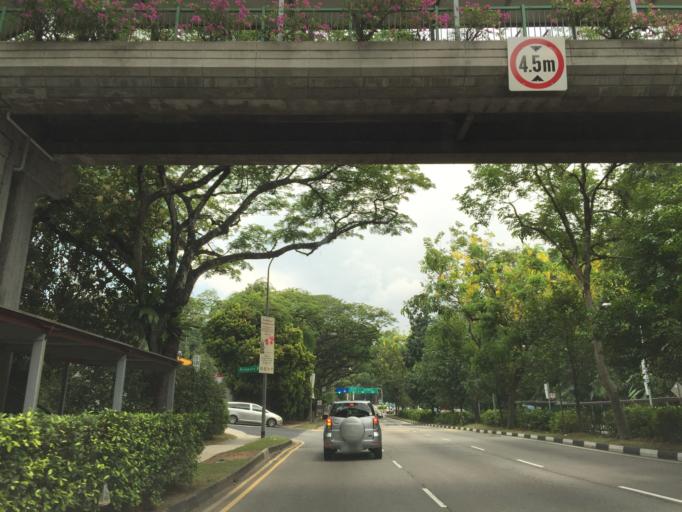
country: SG
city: Singapore
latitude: 1.3075
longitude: 103.8111
